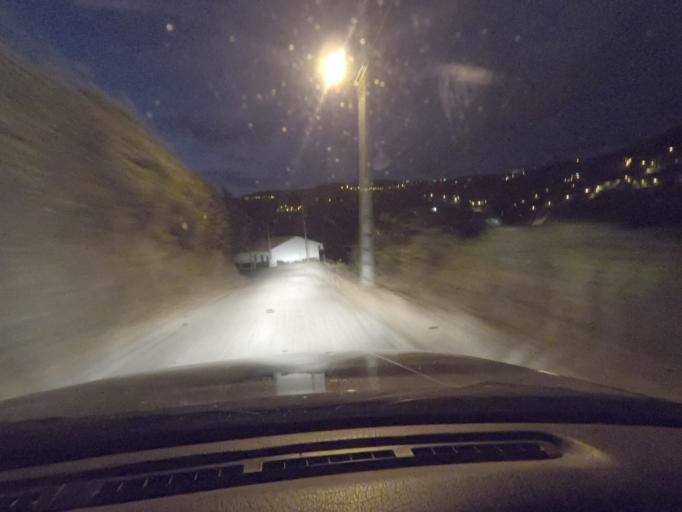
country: PT
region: Vila Real
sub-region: Santa Marta de Penaguiao
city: Santa Marta de Penaguiao
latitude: 41.2027
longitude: -7.8459
